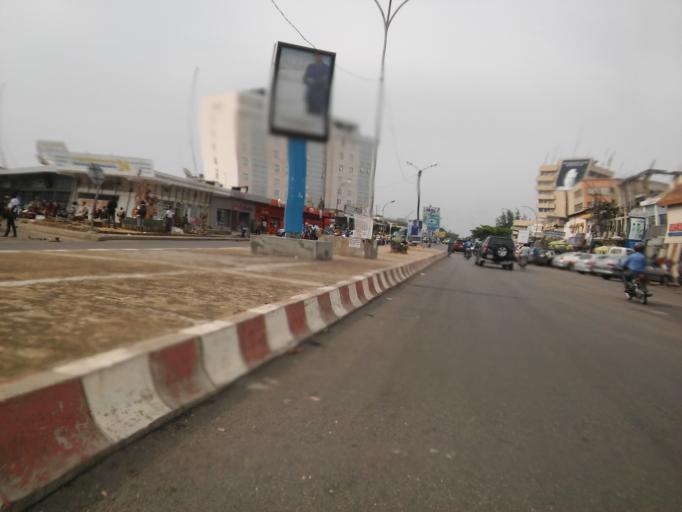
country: BJ
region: Littoral
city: Cotonou
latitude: 6.3556
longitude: 2.4376
